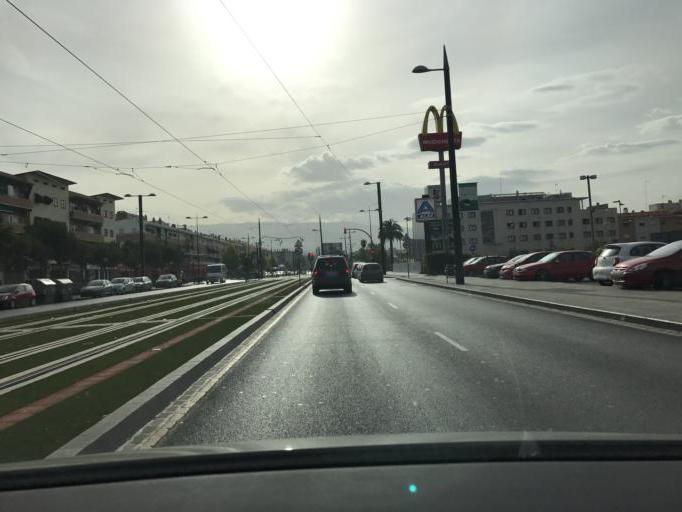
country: ES
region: Andalusia
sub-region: Provincia de Granada
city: Granada
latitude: 37.2021
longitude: -3.6155
